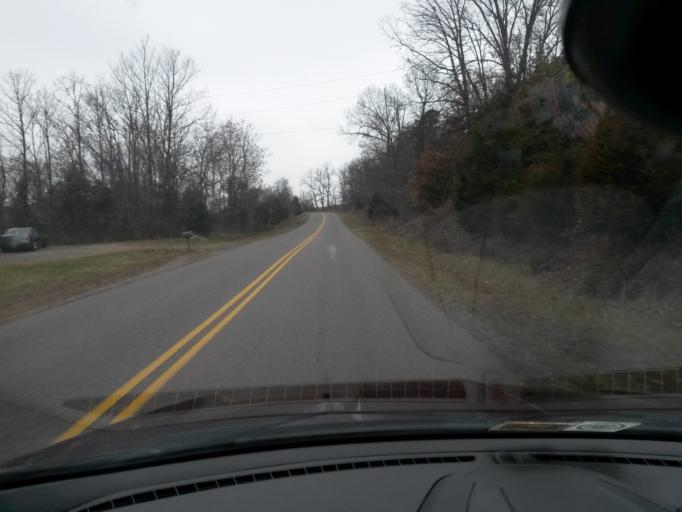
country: US
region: Virginia
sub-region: Rockbridge County
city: East Lexington
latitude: 37.7893
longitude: -79.3757
